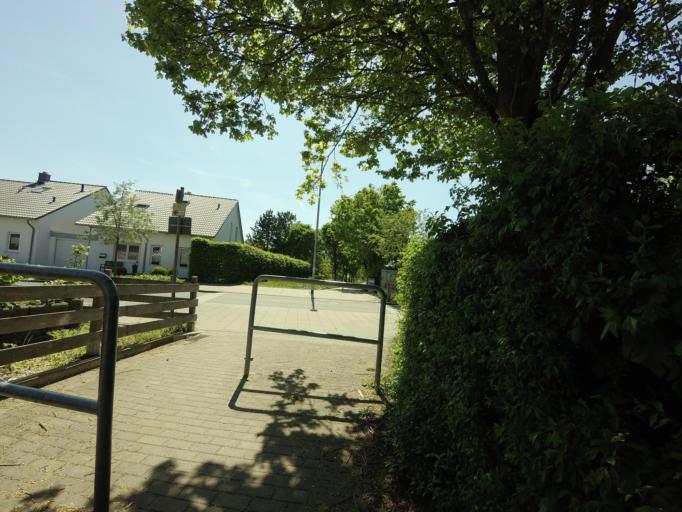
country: DE
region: Lower Saxony
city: Hildesheim
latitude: 52.1260
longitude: 9.9905
